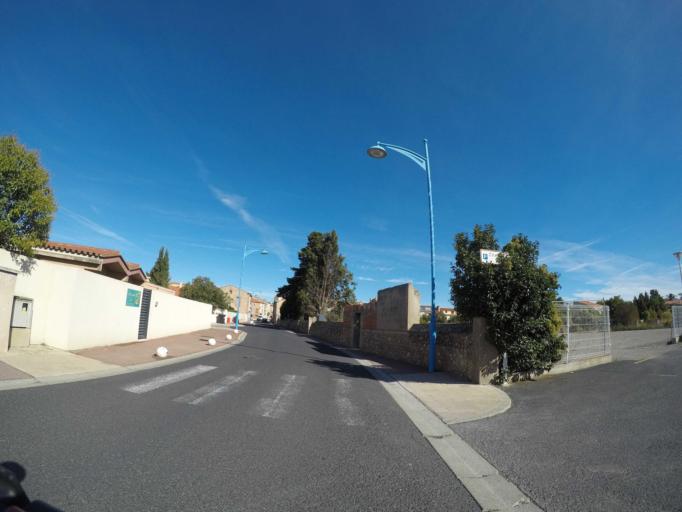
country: FR
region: Languedoc-Roussillon
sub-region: Departement des Pyrenees-Orientales
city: Le Soler
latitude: 42.6803
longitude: 2.7922
